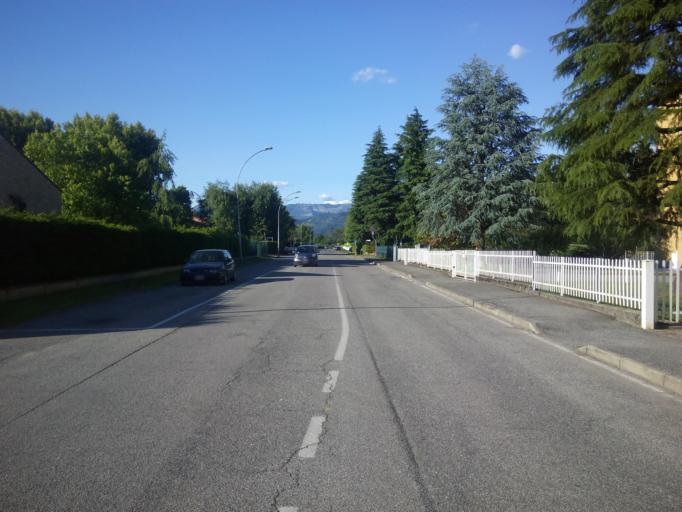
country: IT
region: Lombardy
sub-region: Provincia di Lecco
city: Verderio Superiore
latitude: 45.6678
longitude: 9.4424
